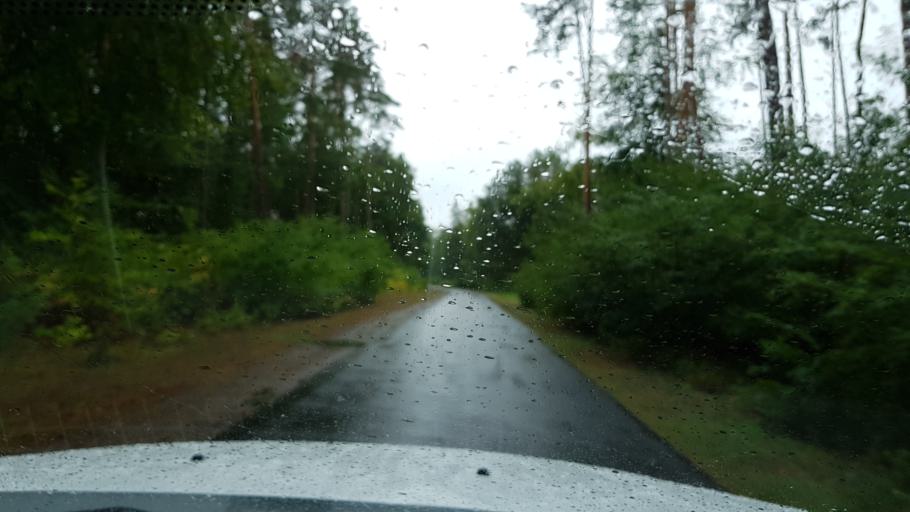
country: DE
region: Brandenburg
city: Schoneberg
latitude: 52.9673
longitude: 14.2056
